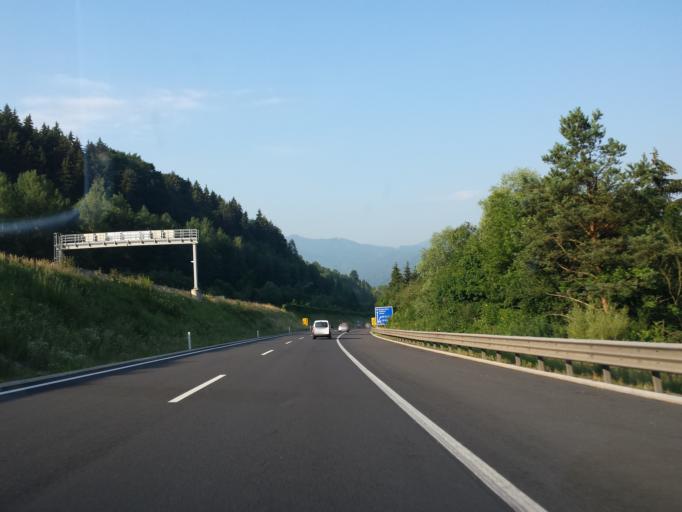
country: AT
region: Styria
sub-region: Politischer Bezirk Bruck-Muerzzuschlag
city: Bruck an der Mur
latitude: 47.4222
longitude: 15.2974
